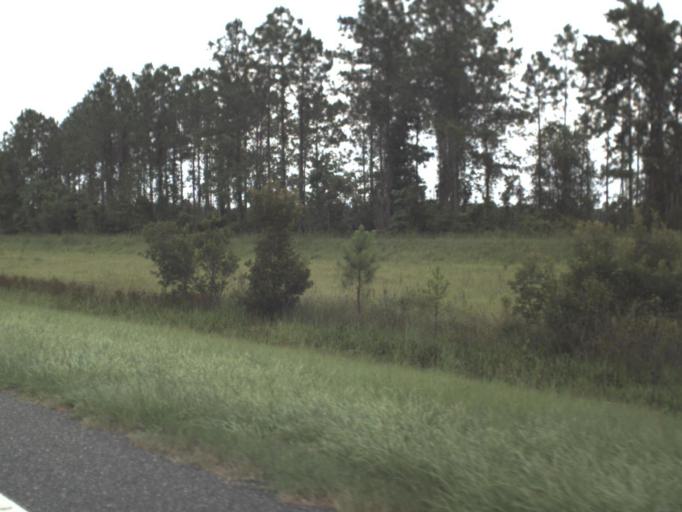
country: US
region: Florida
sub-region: Levy County
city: Bronson
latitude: 29.3140
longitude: -82.7602
